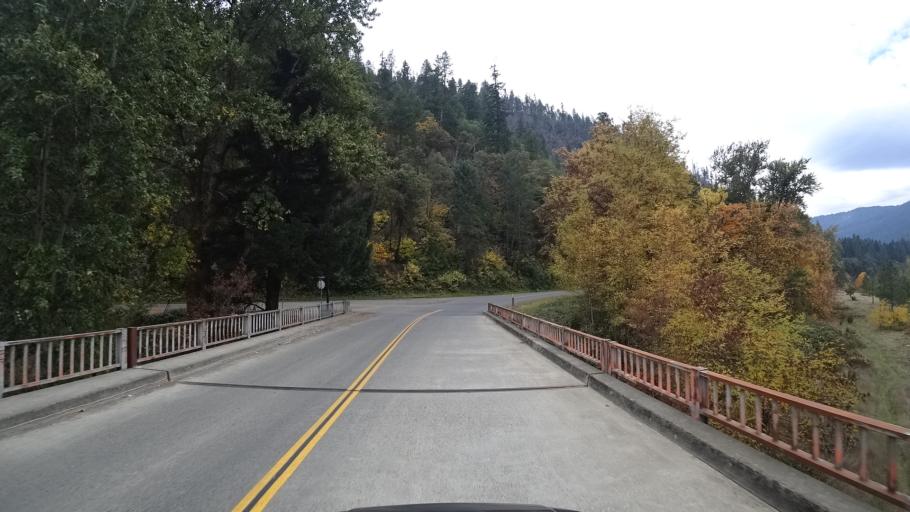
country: US
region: California
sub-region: Siskiyou County
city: Happy Camp
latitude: 41.7897
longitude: -123.3776
